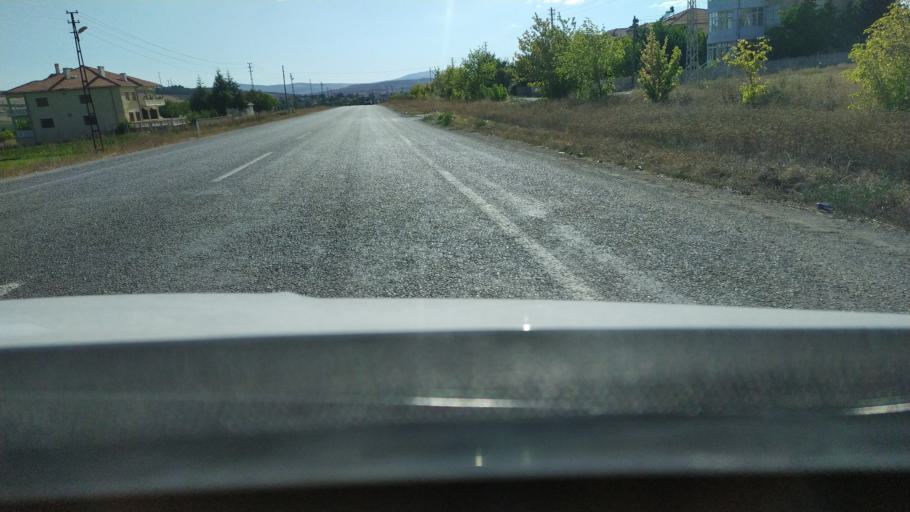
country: TR
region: Kayseri
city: Felahiye
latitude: 39.0985
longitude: 35.5839
